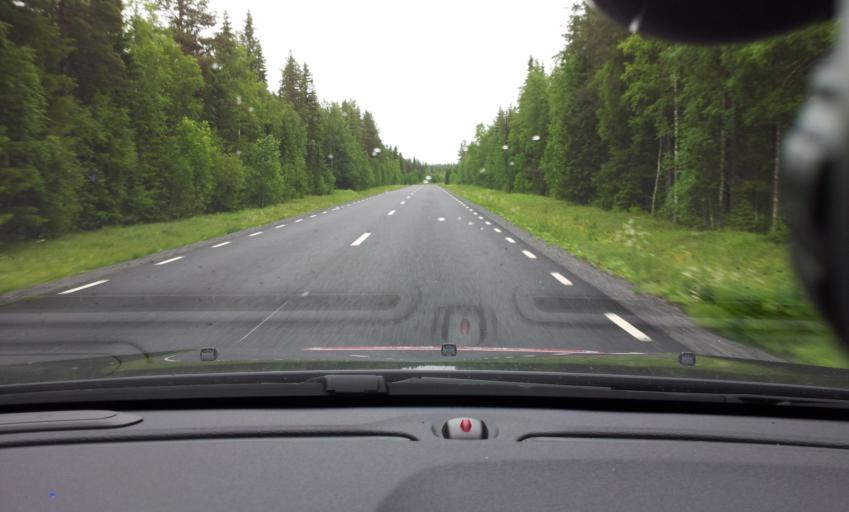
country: SE
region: Jaemtland
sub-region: Stroemsunds Kommun
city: Stroemsund
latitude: 63.6654
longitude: 15.1373
